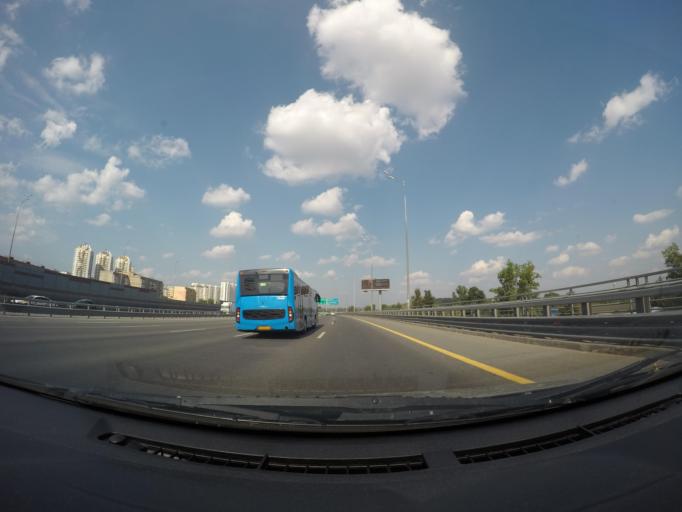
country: RU
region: Moskovskaya
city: Levoberezhnaya
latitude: 55.8914
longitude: 37.4854
